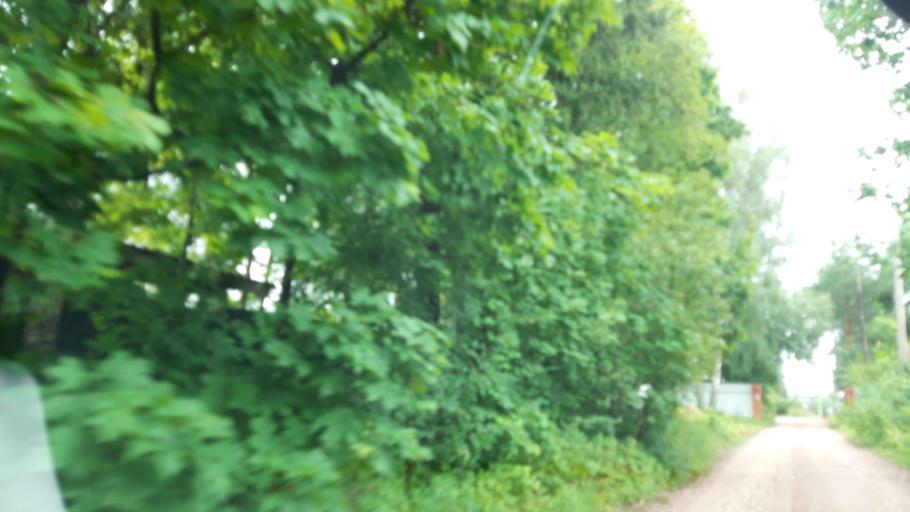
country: RU
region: Tverskaya
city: Konakovo
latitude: 56.6603
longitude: 36.6537
